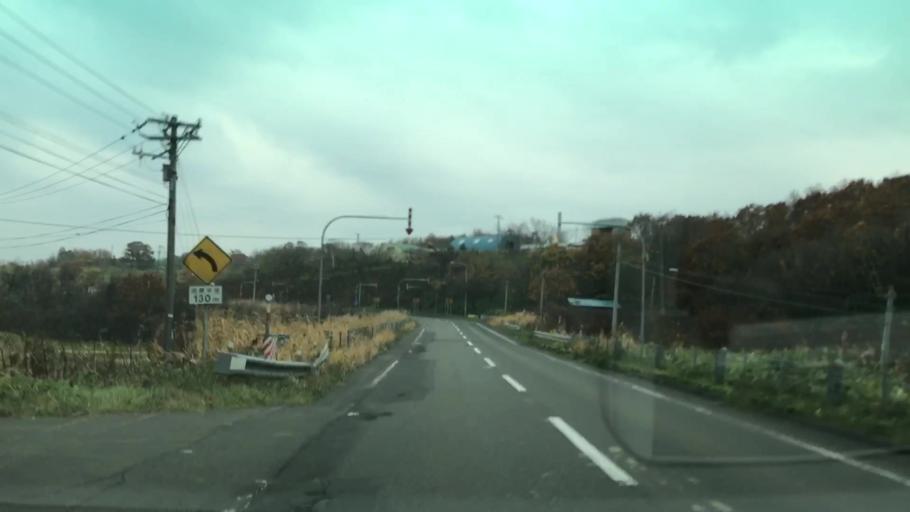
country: JP
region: Hokkaido
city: Ishikari
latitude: 43.3351
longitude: 141.4288
